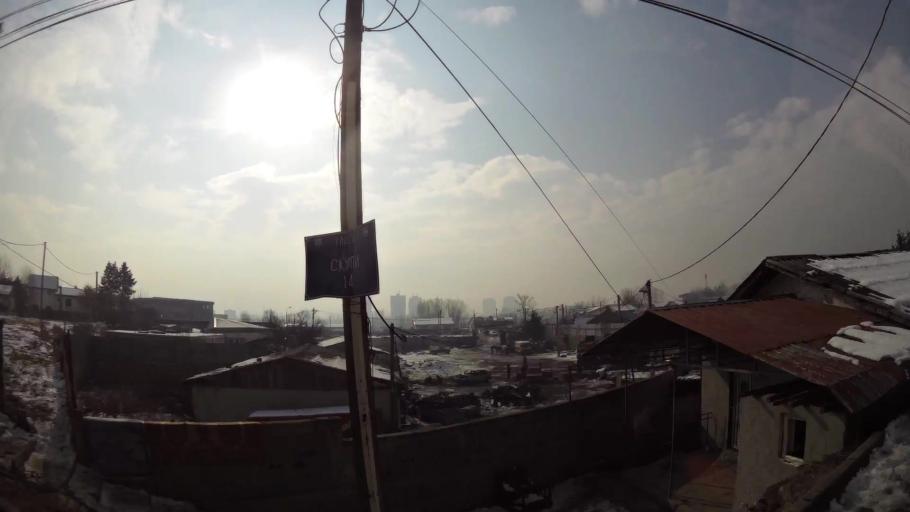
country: MK
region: Suto Orizari
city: Suto Orizare
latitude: 42.0156
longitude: 21.3869
